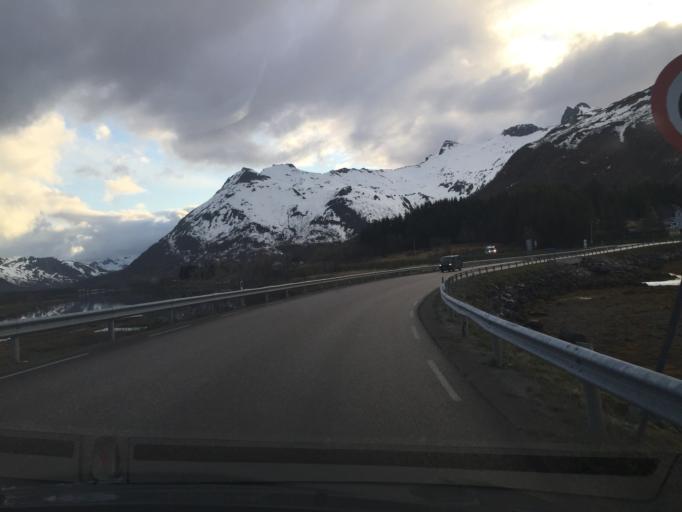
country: NO
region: Nordland
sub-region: Vagan
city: Svolvaer
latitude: 68.3242
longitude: 14.6905
